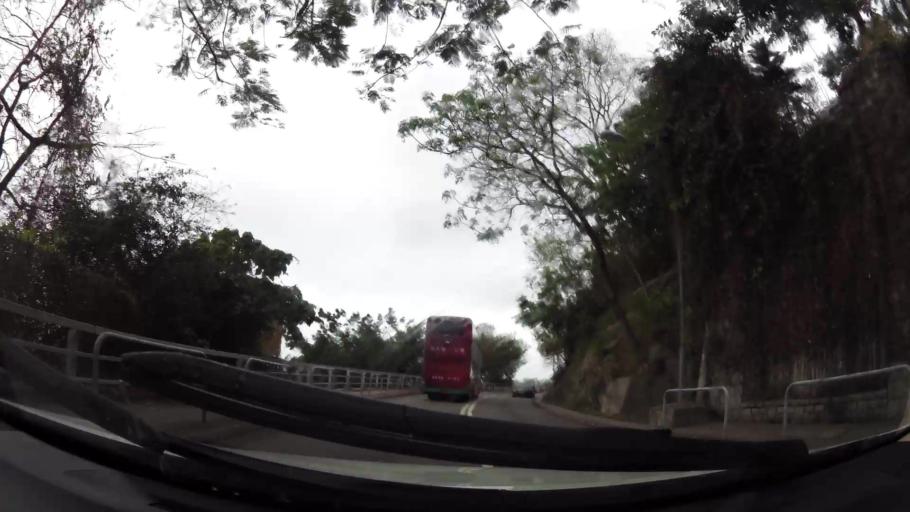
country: HK
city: Hong Kong
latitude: 22.2731
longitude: 114.1193
